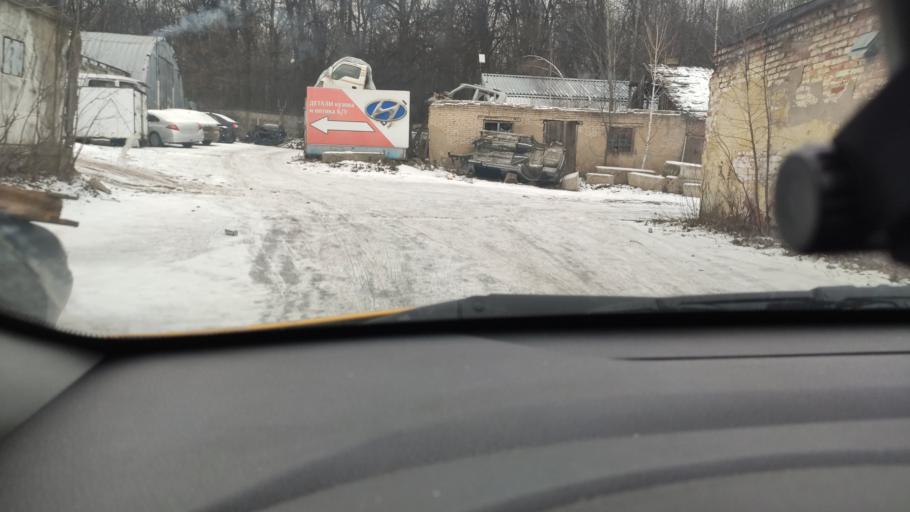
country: RU
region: Moscow
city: Chertanovo Yuzhnoye
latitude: 55.5937
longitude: 37.5791
